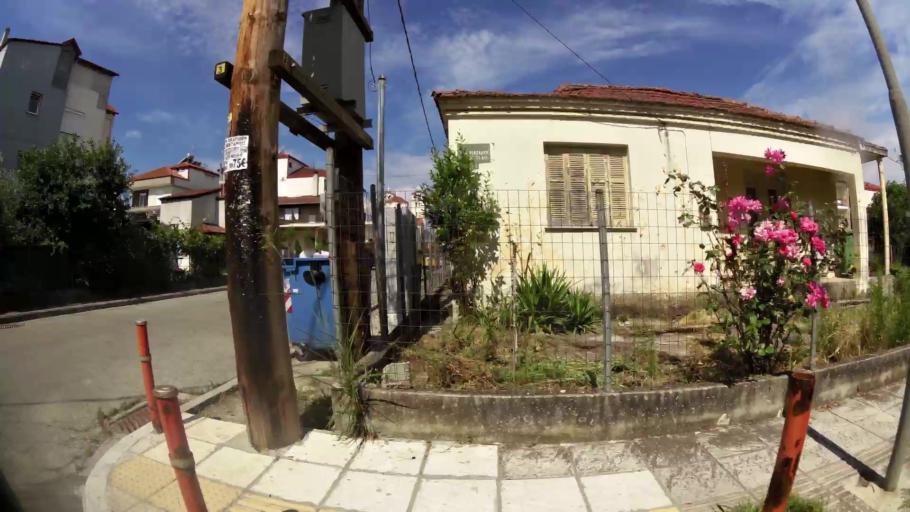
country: GR
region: Central Macedonia
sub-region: Nomos Pierias
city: Katerini
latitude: 40.2642
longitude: 22.4961
